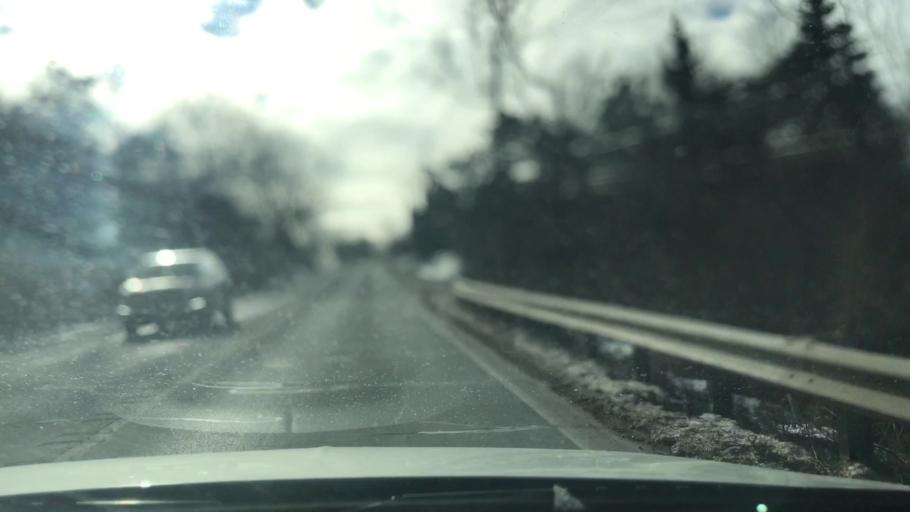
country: US
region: Michigan
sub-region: Oakland County
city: Rochester
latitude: 42.7197
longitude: -83.1533
